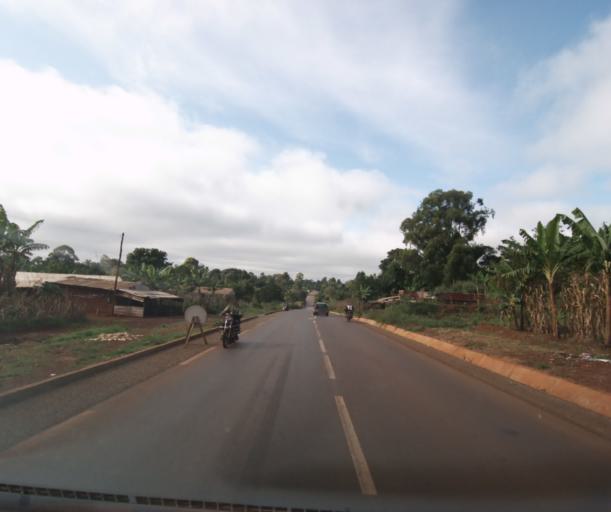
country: CM
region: West
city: Mbouda
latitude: 5.5971
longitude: 10.2940
